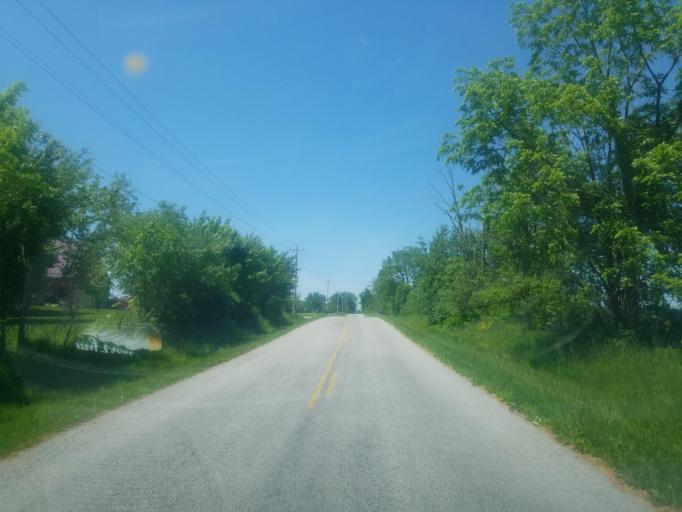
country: US
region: Ohio
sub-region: Huron County
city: New London
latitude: 41.1159
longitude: -82.3522
